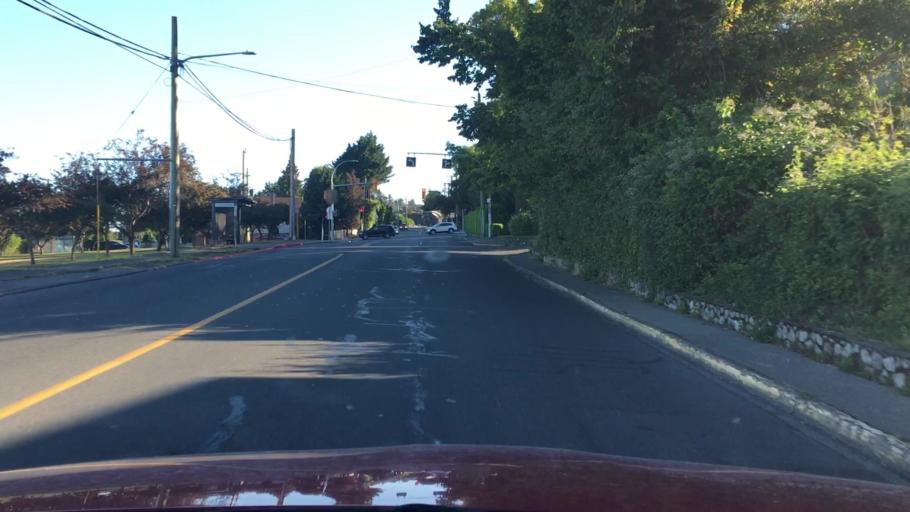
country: CA
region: British Columbia
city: Oak Bay
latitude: 48.4451
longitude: -123.3267
